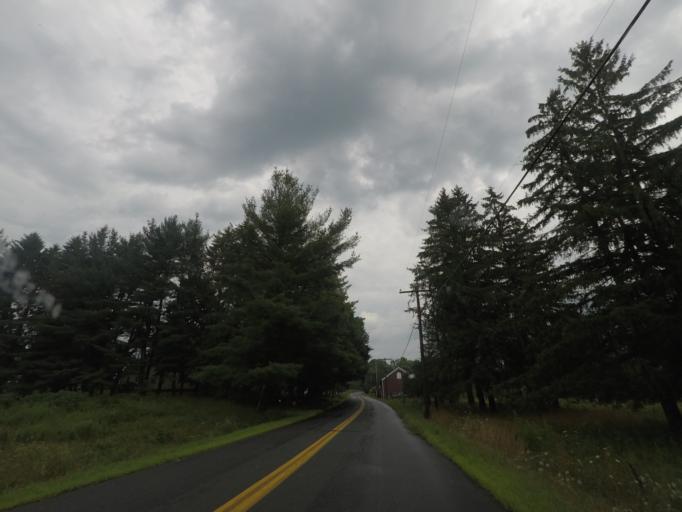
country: US
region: New York
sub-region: Rensselaer County
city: Poestenkill
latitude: 42.7257
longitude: -73.5941
